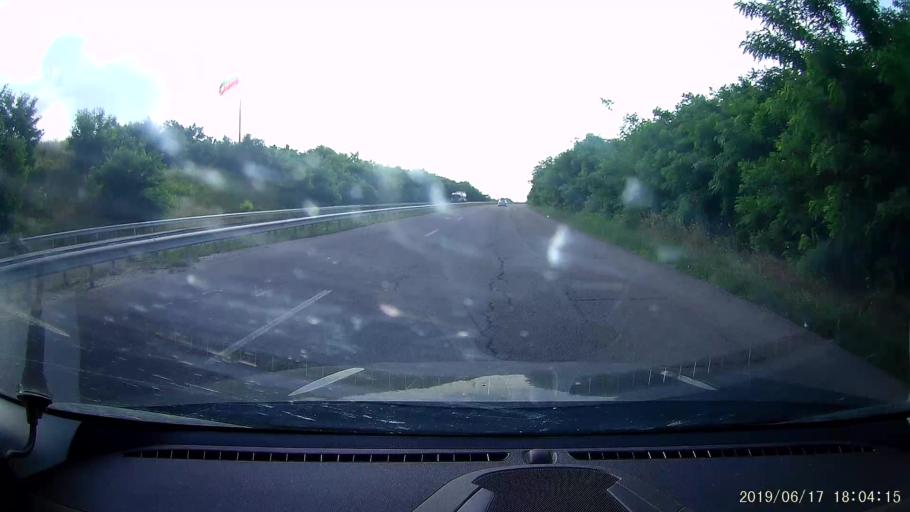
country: BG
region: Khaskovo
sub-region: Obshtina Svilengrad
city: Svilengrad
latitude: 41.7841
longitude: 26.2020
